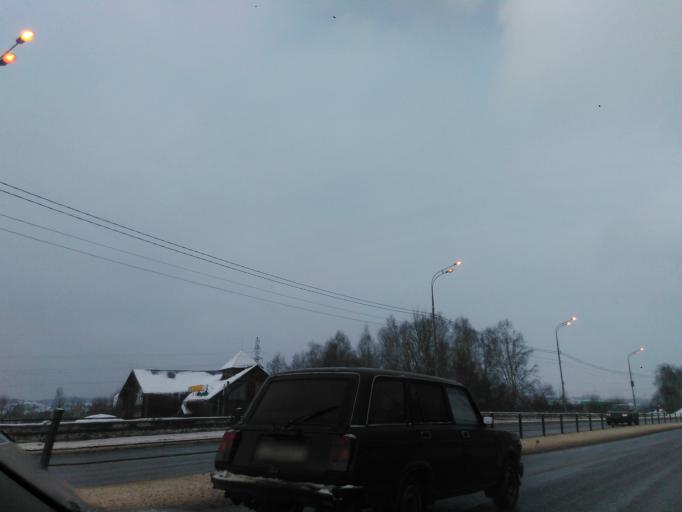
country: RU
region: Moskovskaya
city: Dedenevo
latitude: 56.2618
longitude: 37.5044
